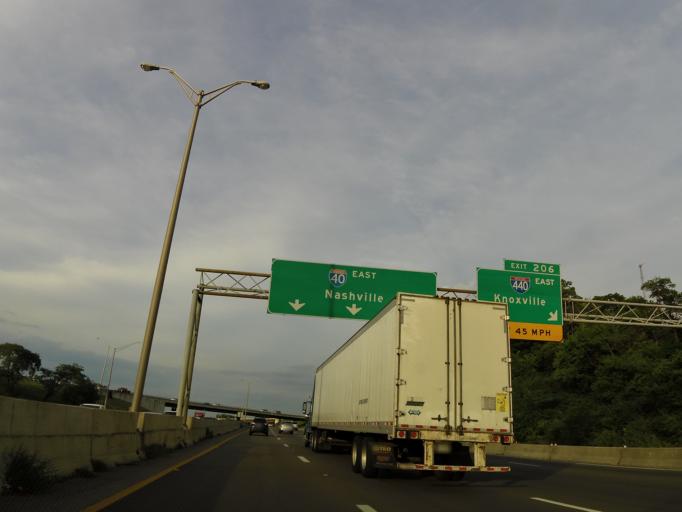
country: US
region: Tennessee
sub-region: Davidson County
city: Nashville
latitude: 36.1559
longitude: -86.8271
